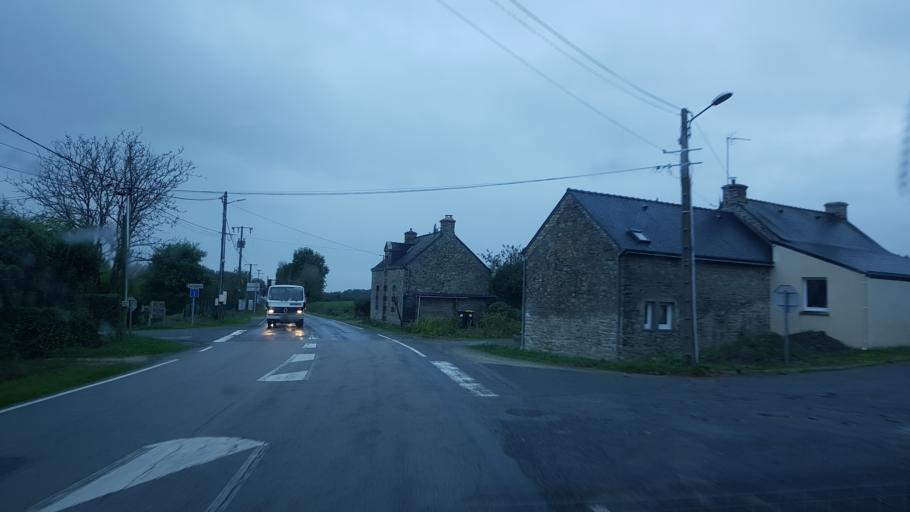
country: FR
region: Brittany
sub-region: Departement du Morbihan
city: Trefflean
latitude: 47.6763
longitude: -2.6065
